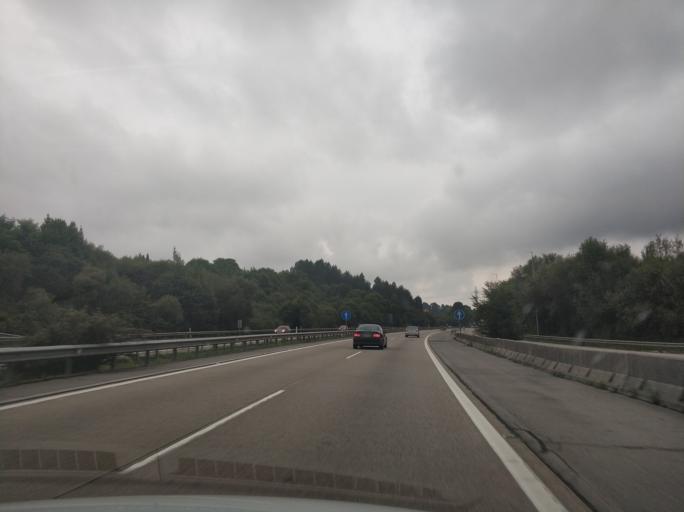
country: ES
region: Asturias
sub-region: Province of Asturias
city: Corvera de Asturias
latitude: 43.5153
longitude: -5.8208
